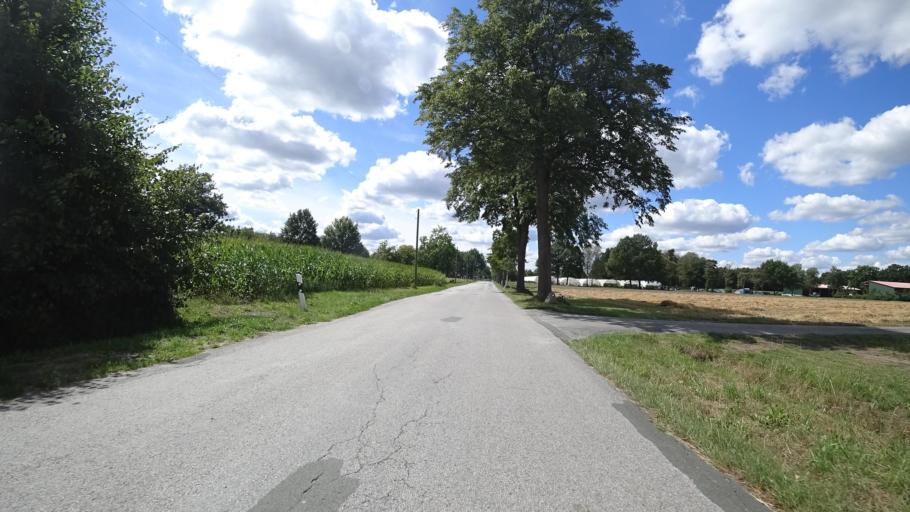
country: DE
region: North Rhine-Westphalia
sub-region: Regierungsbezirk Detmold
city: Steinhagen
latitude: 51.9625
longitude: 8.4327
